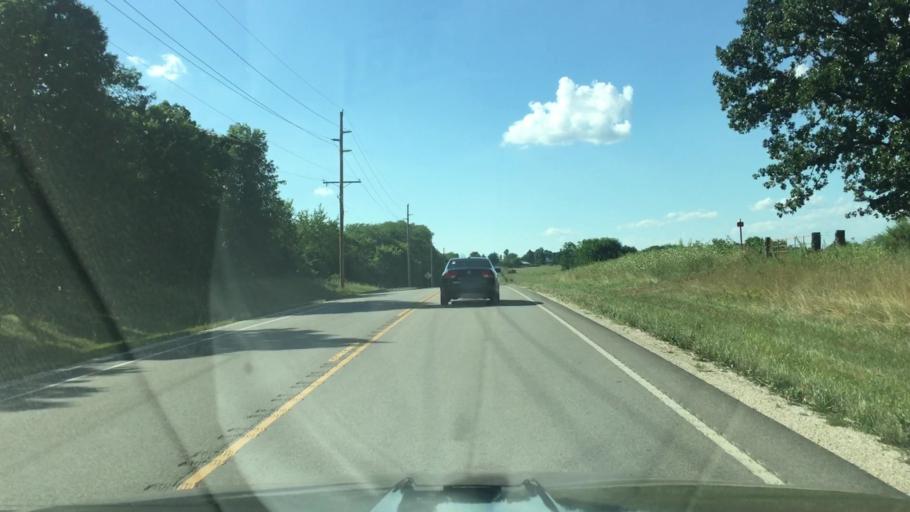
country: US
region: Missouri
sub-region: Morgan County
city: Versailles
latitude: 38.4347
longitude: -92.7822
